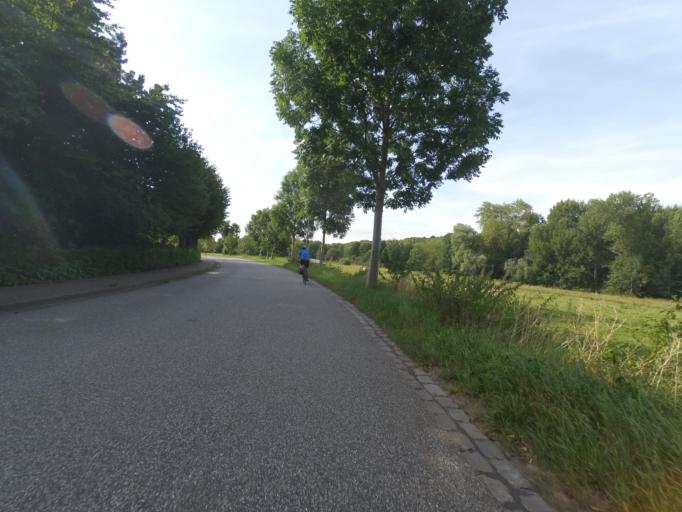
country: DE
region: Schleswig-Holstein
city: Oststeinbek
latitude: 53.5046
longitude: 10.1698
